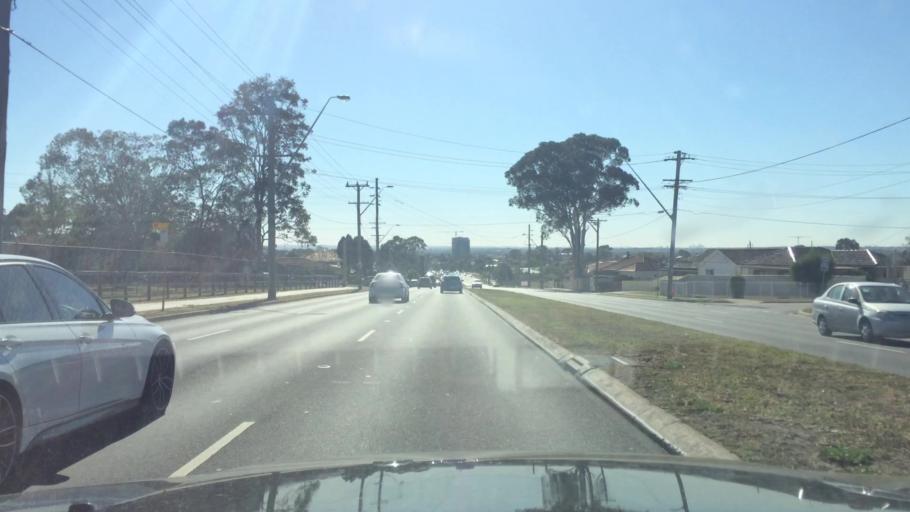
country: AU
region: New South Wales
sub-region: Campbelltown Municipality
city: Glenfield
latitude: -33.9488
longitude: 150.9063
